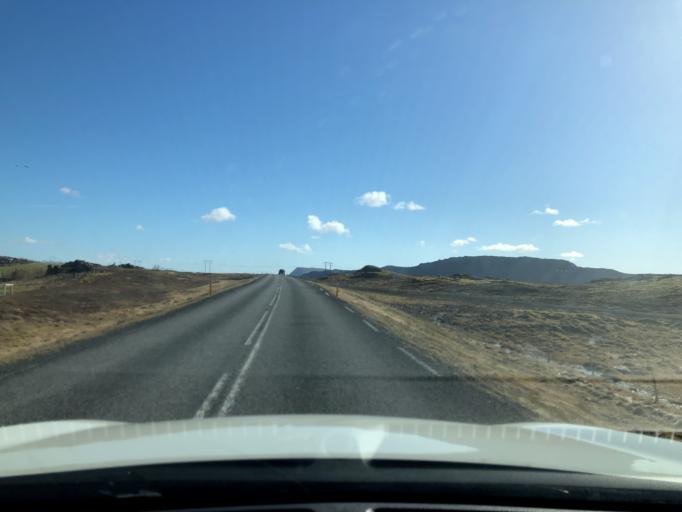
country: IS
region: West
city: Borgarnes
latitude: 64.5601
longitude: -21.7194
